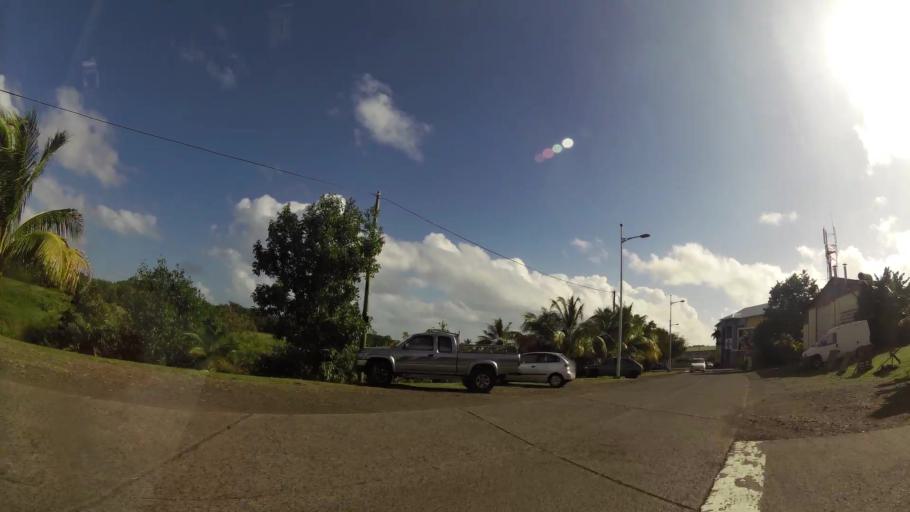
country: MQ
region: Martinique
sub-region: Martinique
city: Le Francois
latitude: 14.6163
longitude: -60.9030
